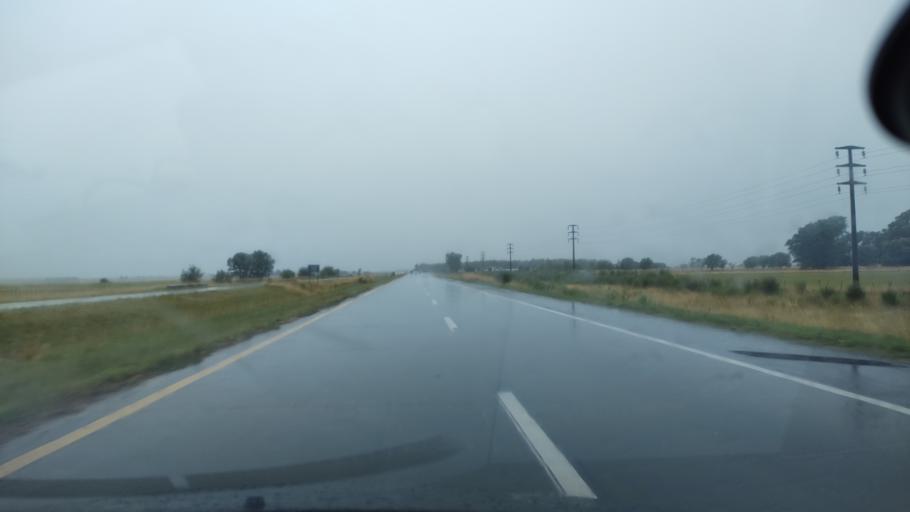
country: AR
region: Buenos Aires
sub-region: Partido de San Vicente
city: San Vicente
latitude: -35.0679
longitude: -58.5021
